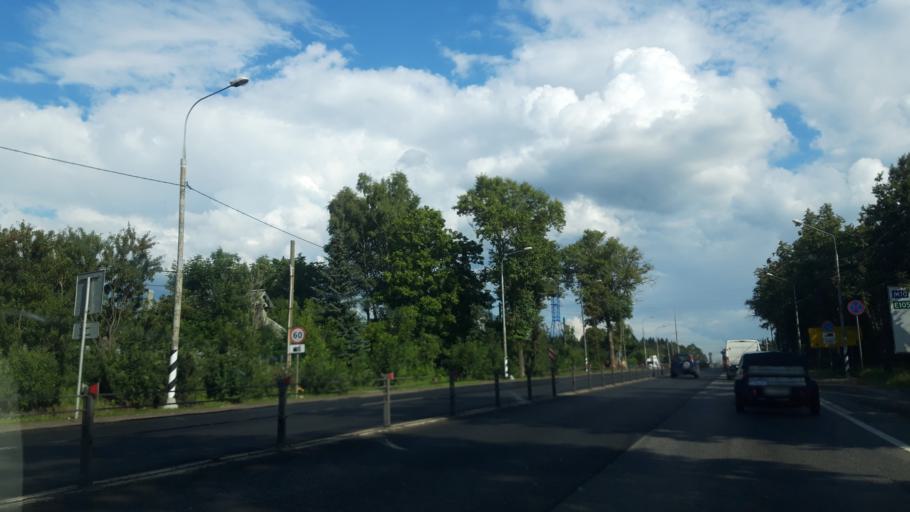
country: RU
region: Moskovskaya
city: Klin
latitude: 56.2807
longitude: 36.8269
